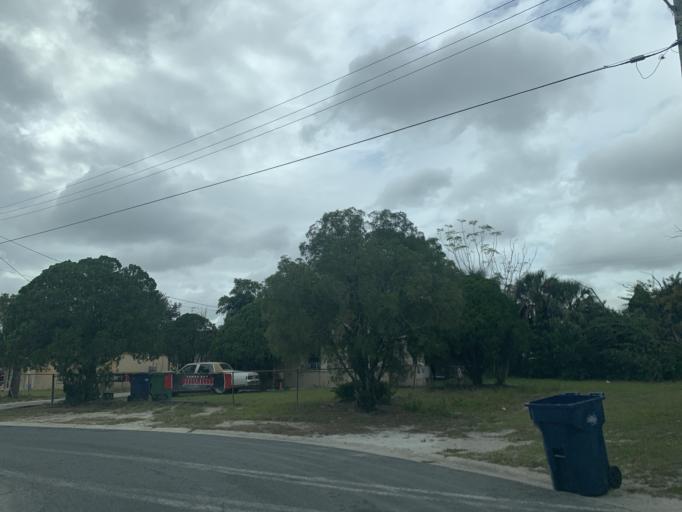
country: US
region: Florida
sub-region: Hillsborough County
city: East Lake-Orient Park
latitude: 27.9756
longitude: -82.4053
